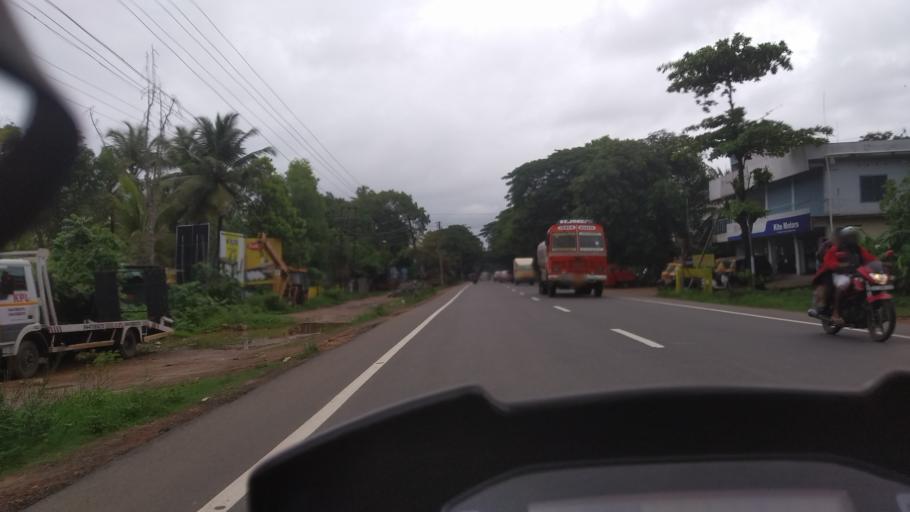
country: IN
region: Kerala
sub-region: Alappuzha
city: Alleppey
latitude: 9.4560
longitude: 76.3408
